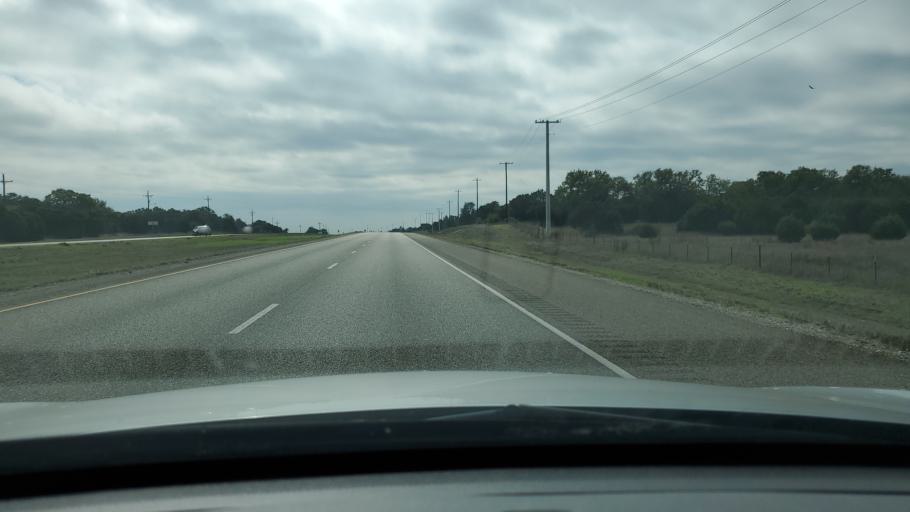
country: US
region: Texas
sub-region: Williamson County
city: Florence
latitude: 30.7995
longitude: -97.7685
